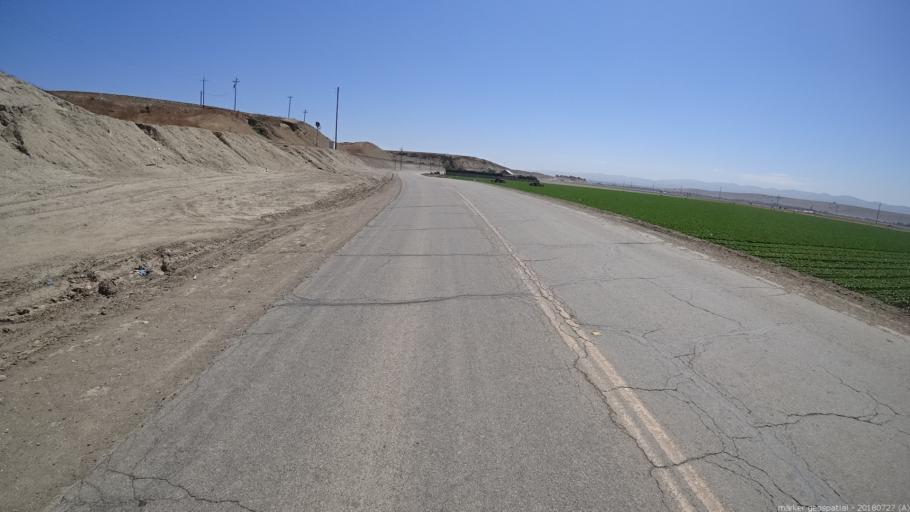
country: US
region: California
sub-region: Monterey County
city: King City
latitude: 36.1829
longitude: -121.0625
